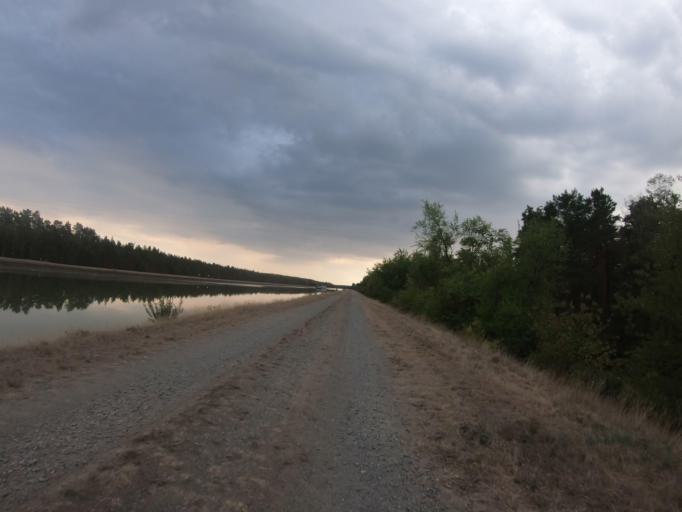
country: DE
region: Lower Saxony
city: Sassenburg
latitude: 52.5498
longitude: 10.6594
